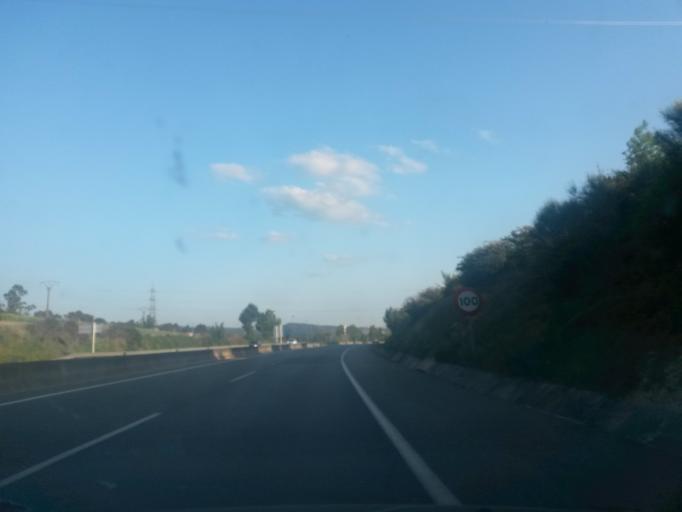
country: ES
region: Catalonia
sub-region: Provincia de Girona
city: Palol de Revardit
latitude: 42.0539
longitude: 2.8175
